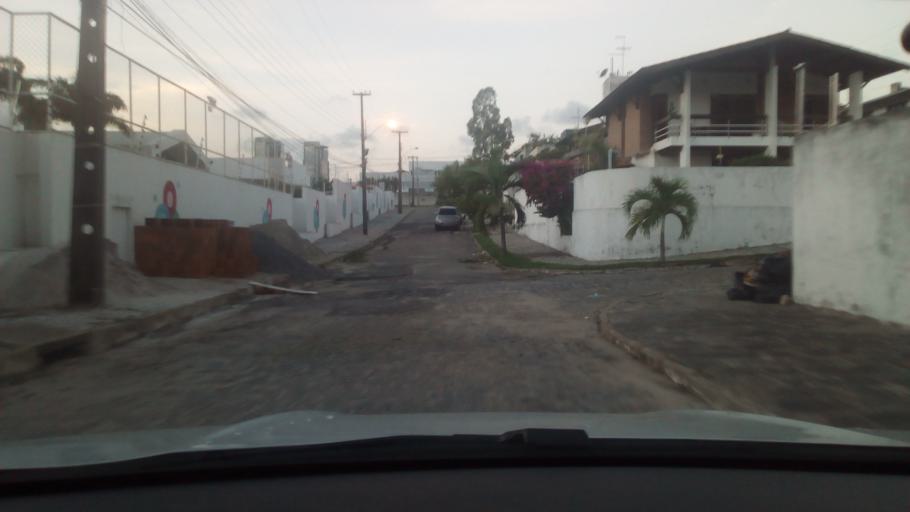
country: BR
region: Paraiba
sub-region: Joao Pessoa
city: Joao Pessoa
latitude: -7.1119
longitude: -34.8437
